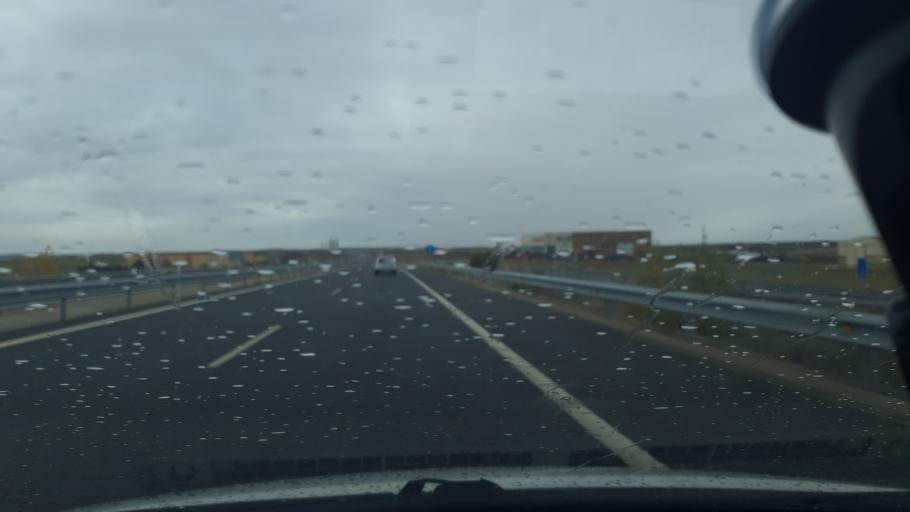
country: ES
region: Castille and Leon
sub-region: Provincia de Segovia
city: Encinillas
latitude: 41.0029
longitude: -4.1545
